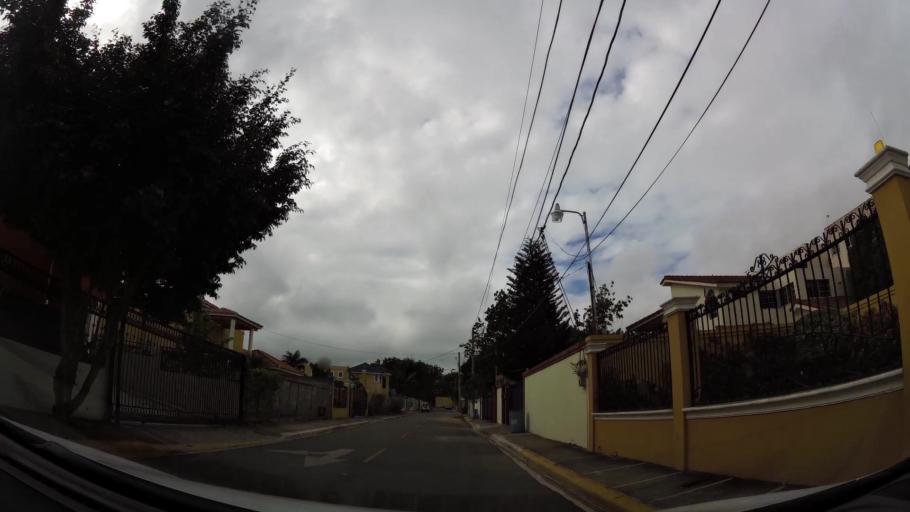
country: DO
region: Santiago
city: Santiago de los Caballeros
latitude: 19.4651
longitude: -70.6594
